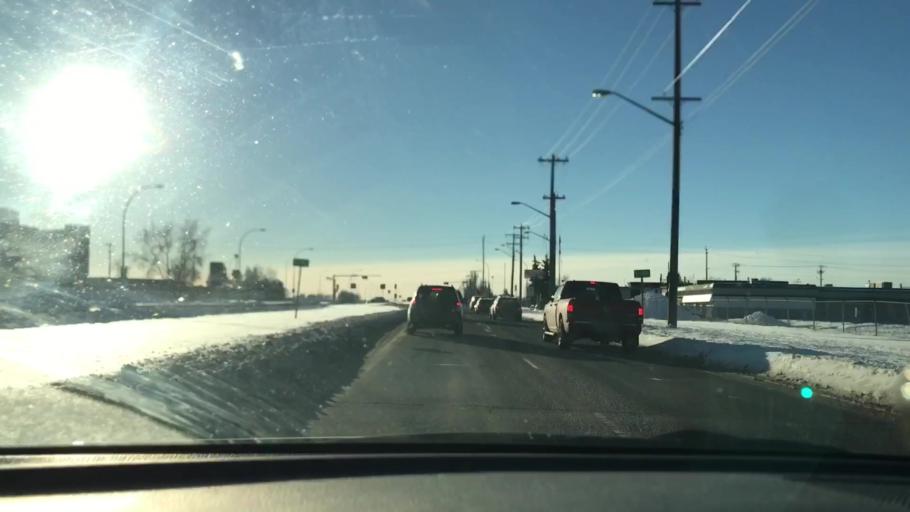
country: CA
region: Alberta
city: Edmonton
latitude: 53.4900
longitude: -113.4673
